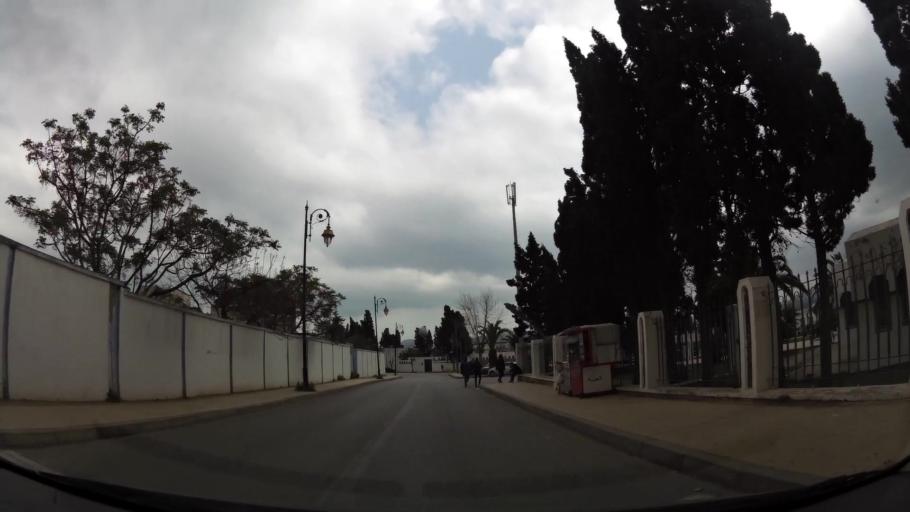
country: MA
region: Tanger-Tetouan
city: Tetouan
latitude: 35.5626
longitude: -5.3636
